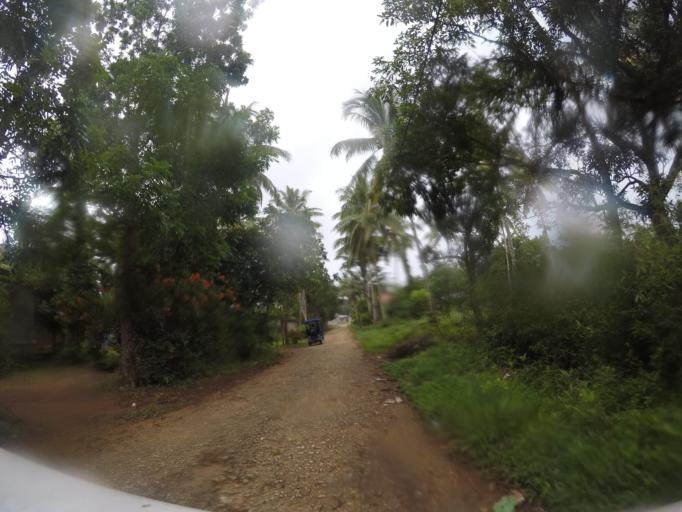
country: TL
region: Lautem
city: Lospalos
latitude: -8.5264
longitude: 126.9945
